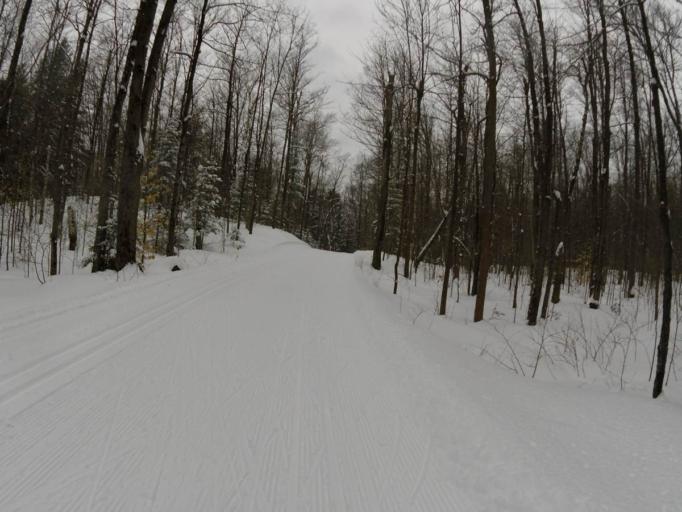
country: CA
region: Quebec
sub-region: Outaouais
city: Wakefield
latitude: 45.5926
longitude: -76.0110
